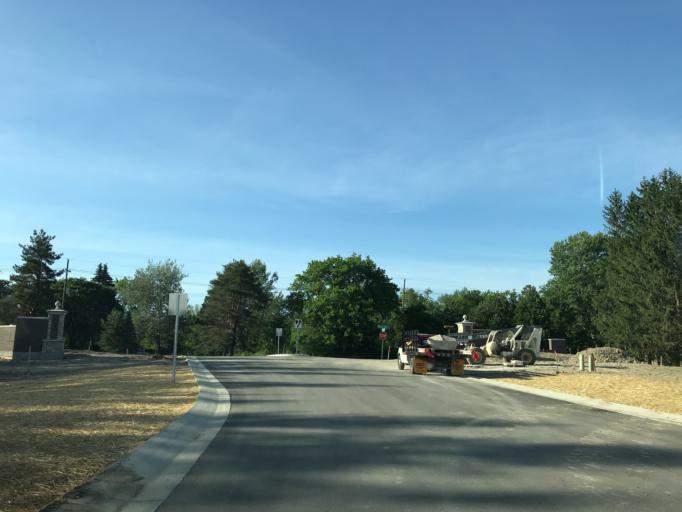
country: US
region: Michigan
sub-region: Oakland County
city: Novi
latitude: 42.4790
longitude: -83.5217
